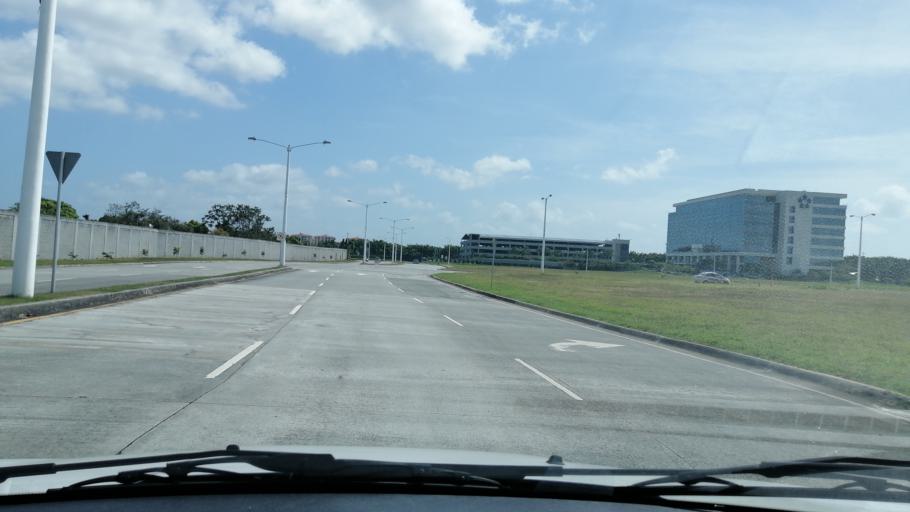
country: PA
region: Panama
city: San Miguelito
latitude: 9.0397
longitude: -79.4261
